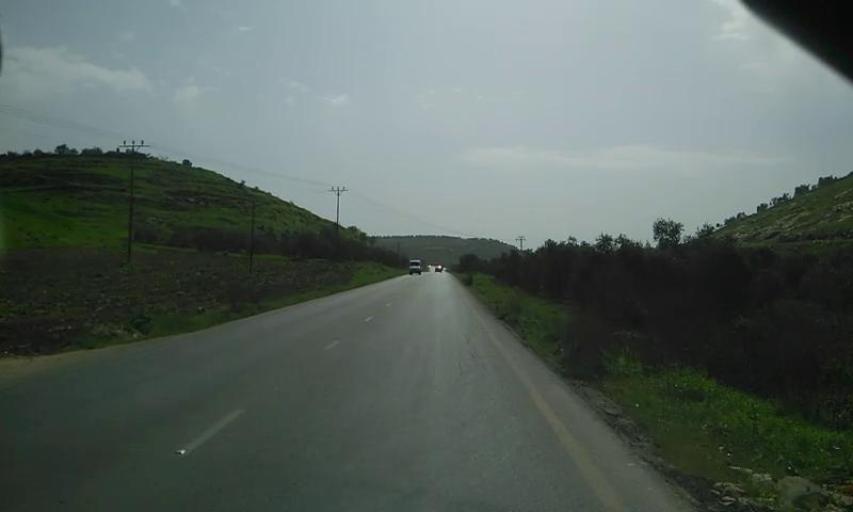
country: PS
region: West Bank
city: Mirkah
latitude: 32.3908
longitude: 35.2180
